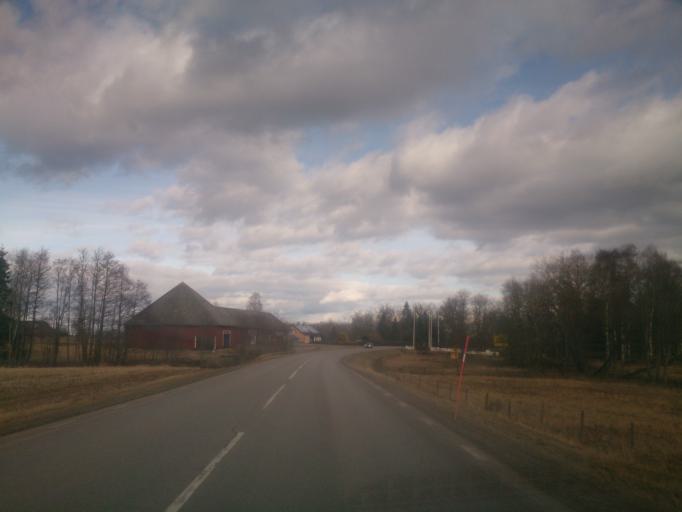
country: SE
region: OEstergoetland
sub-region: Motala Kommun
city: Stenstorp
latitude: 58.5194
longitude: 15.1268
